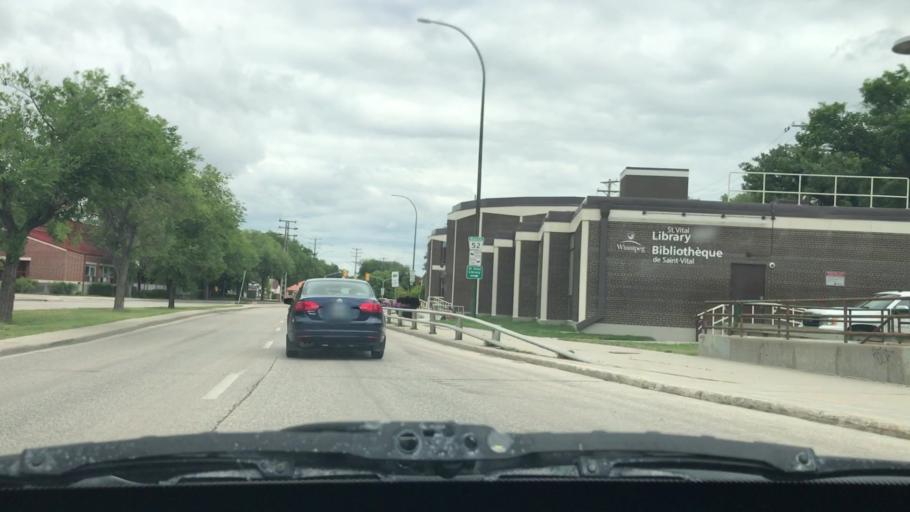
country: CA
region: Manitoba
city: Winnipeg
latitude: 49.8517
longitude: -97.1141
